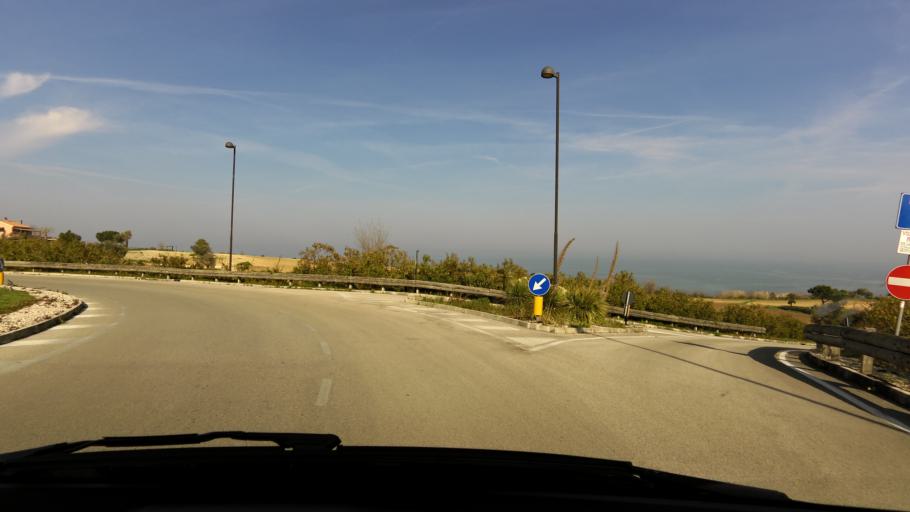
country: IT
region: The Marches
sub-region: Provincia di Ancona
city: Numana
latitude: 43.5032
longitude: 13.6179
